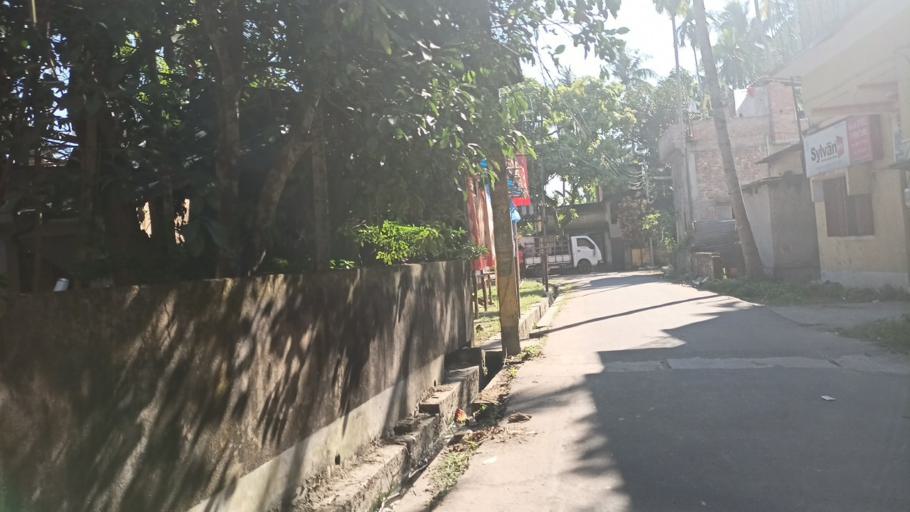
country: IN
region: West Bengal
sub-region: North 24 Parganas
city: Bangaon
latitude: 23.0509
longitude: 88.8242
